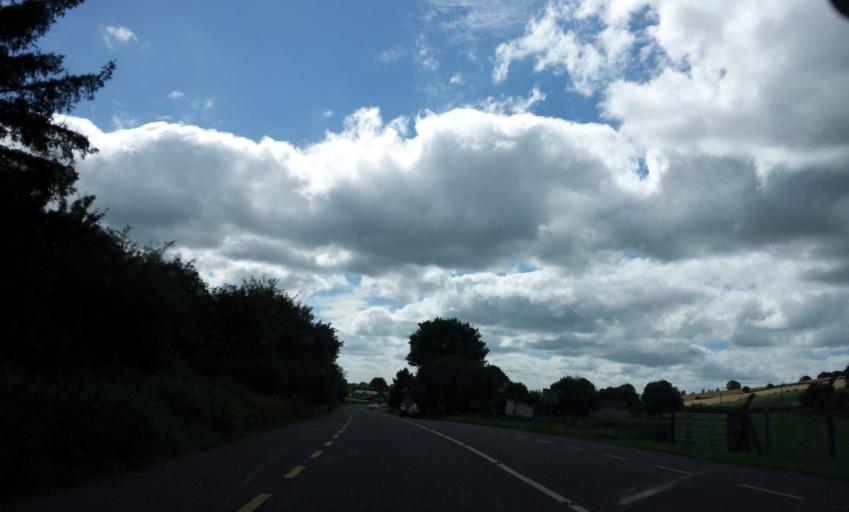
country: IE
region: Munster
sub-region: County Cork
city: Killumney
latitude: 51.8798
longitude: -8.6908
